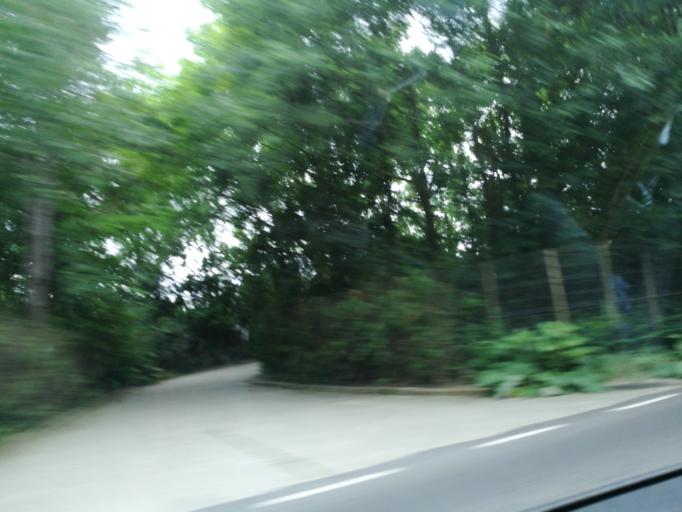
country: RO
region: Constanta
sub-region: Comuna Douazeci si Trei August
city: Douazeci si Trei August
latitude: 43.8750
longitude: 28.5968
